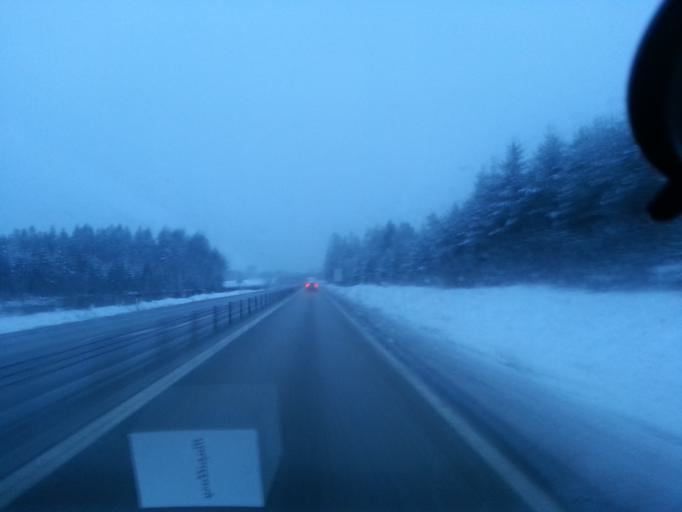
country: SE
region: Kronoberg
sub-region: Ljungby Kommun
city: Lagan
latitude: 56.9973
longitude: 14.0294
